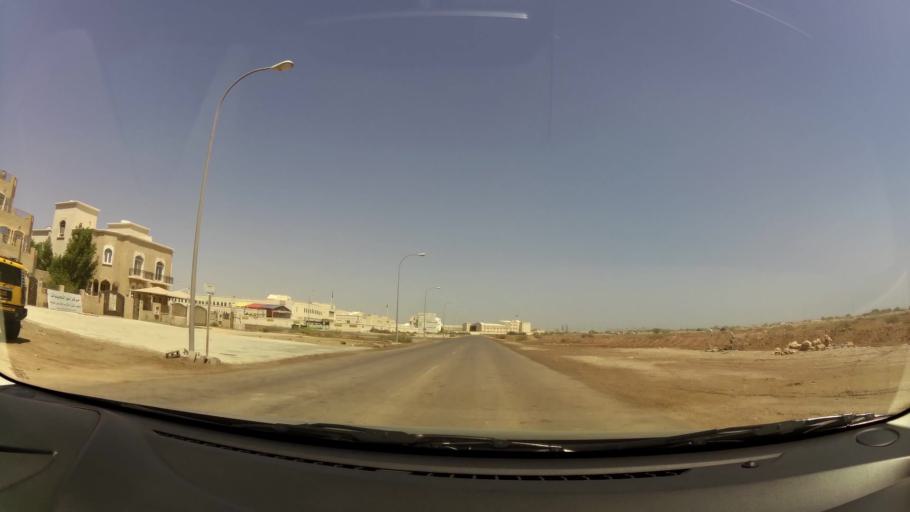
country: OM
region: Muhafazat Masqat
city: As Sib al Jadidah
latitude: 23.6268
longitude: 58.2553
